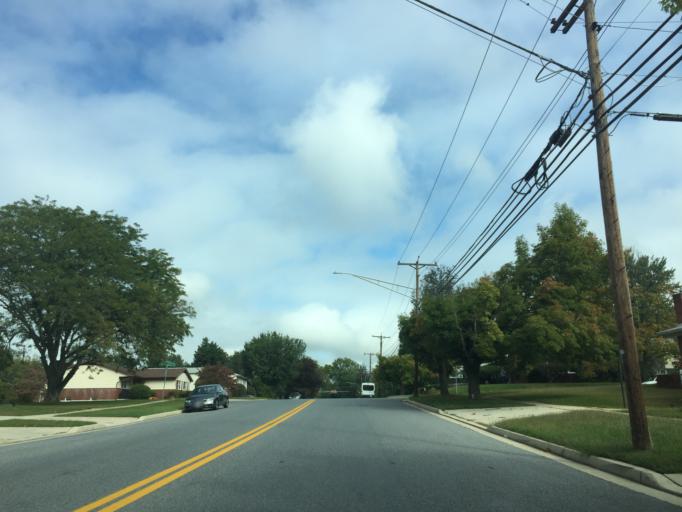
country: US
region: Maryland
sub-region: Baltimore County
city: Pikesville
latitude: 39.3729
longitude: -76.6823
